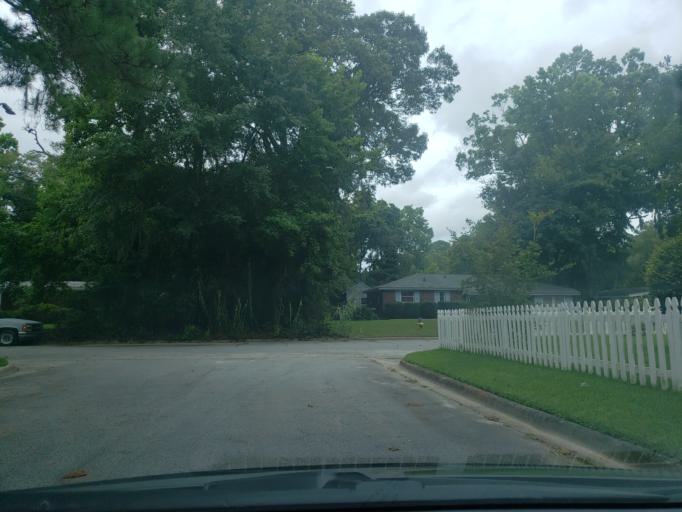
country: US
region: Georgia
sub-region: Chatham County
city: Montgomery
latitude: 31.9938
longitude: -81.1226
